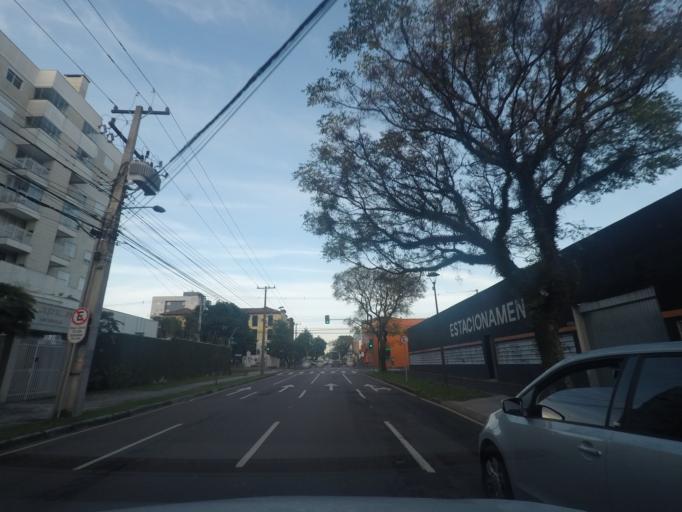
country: BR
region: Parana
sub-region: Curitiba
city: Curitiba
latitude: -25.4431
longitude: -49.2626
